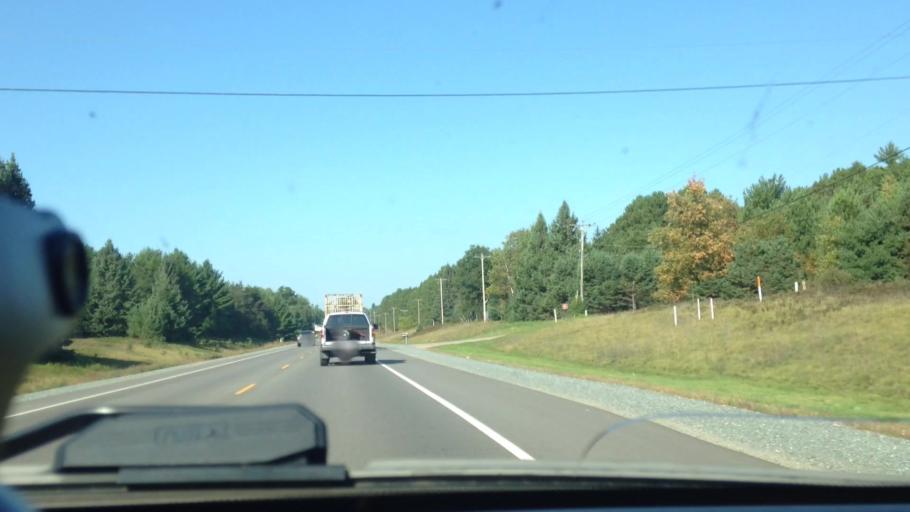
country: US
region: Michigan
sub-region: Dickinson County
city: Iron Mountain
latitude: 45.8760
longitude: -88.0986
